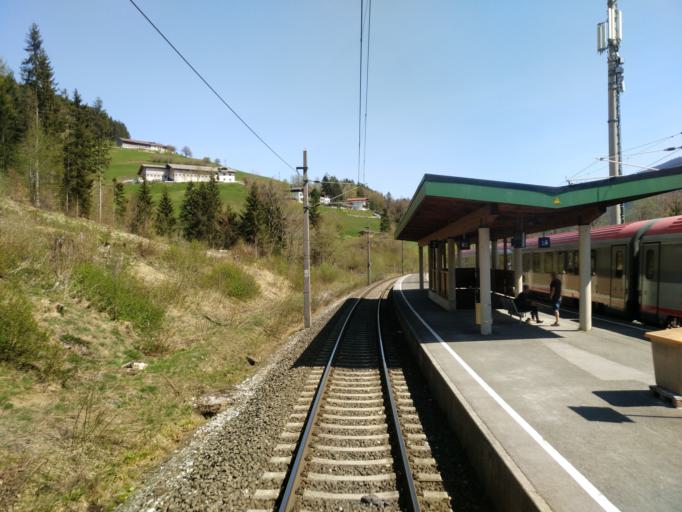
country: AT
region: Salzburg
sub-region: Politischer Bezirk Zell am See
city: Leogang
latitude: 47.4435
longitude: 12.7401
